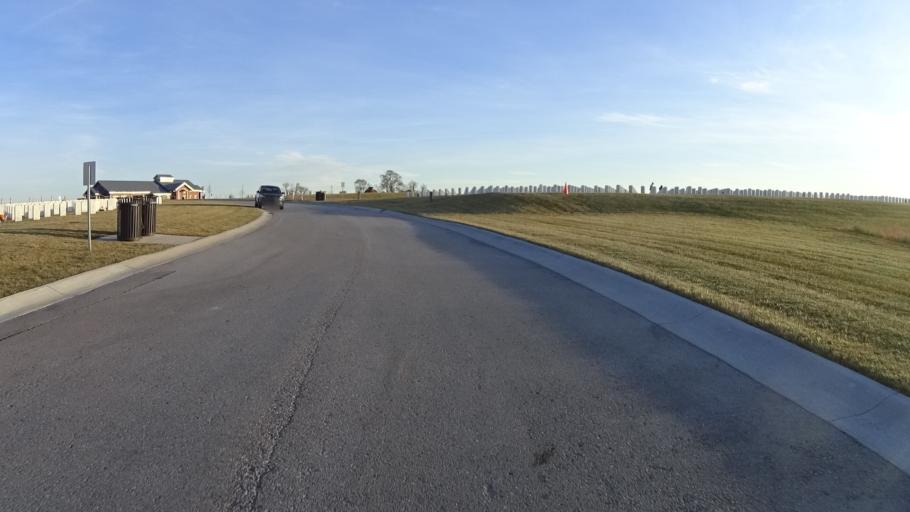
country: US
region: Nebraska
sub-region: Sarpy County
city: Chalco
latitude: 41.1356
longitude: -96.1342
